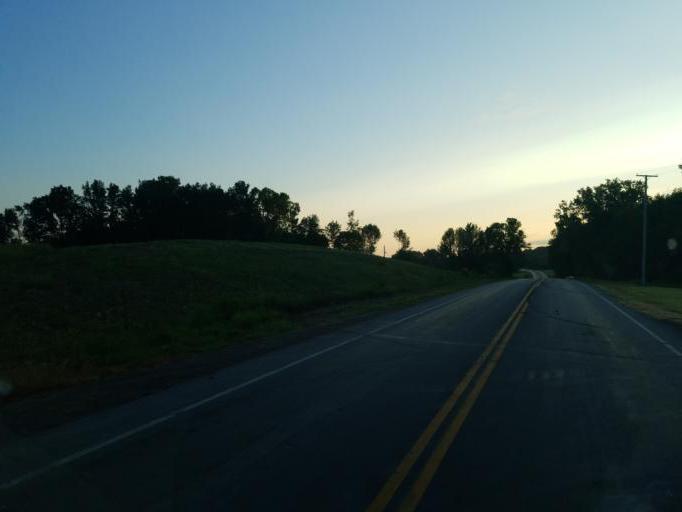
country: US
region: New York
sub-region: Wayne County
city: Clyde
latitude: 43.0576
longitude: -76.8970
